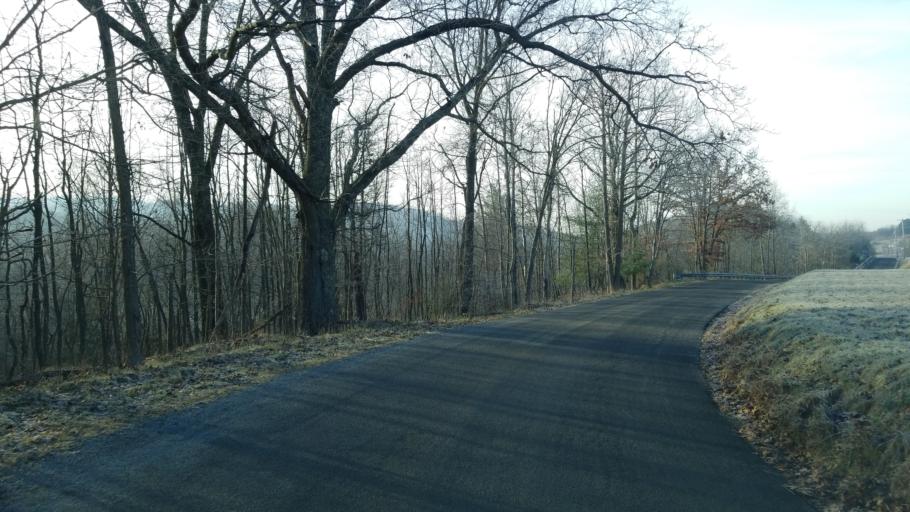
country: US
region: Pennsylvania
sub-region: Jefferson County
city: Brookville
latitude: 40.9550
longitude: -79.2637
